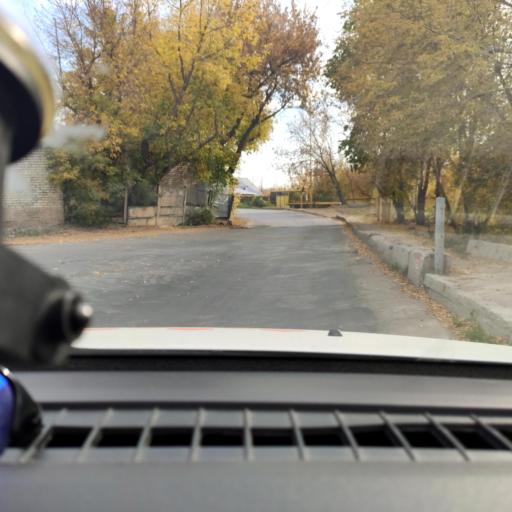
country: RU
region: Samara
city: Samara
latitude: 53.1778
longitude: 50.1475
